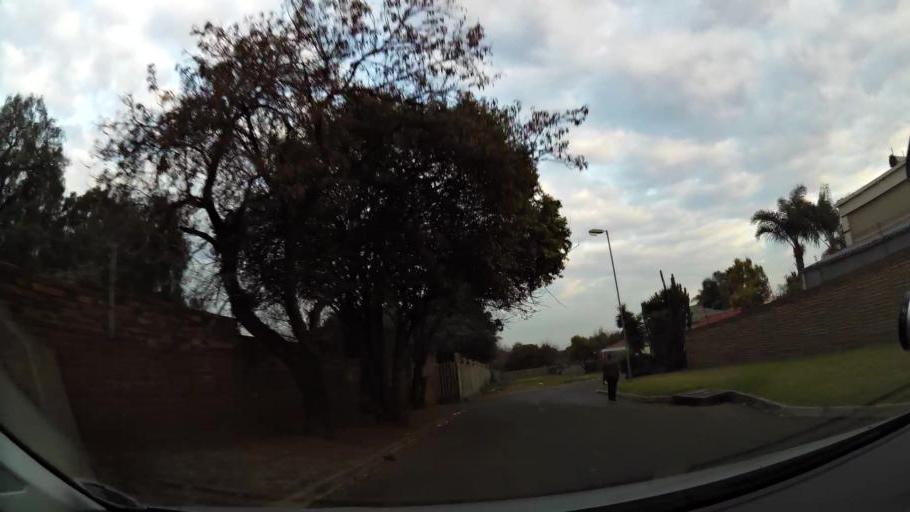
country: ZA
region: Gauteng
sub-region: Ekurhuleni Metropolitan Municipality
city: Germiston
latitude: -26.1926
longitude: 28.1546
